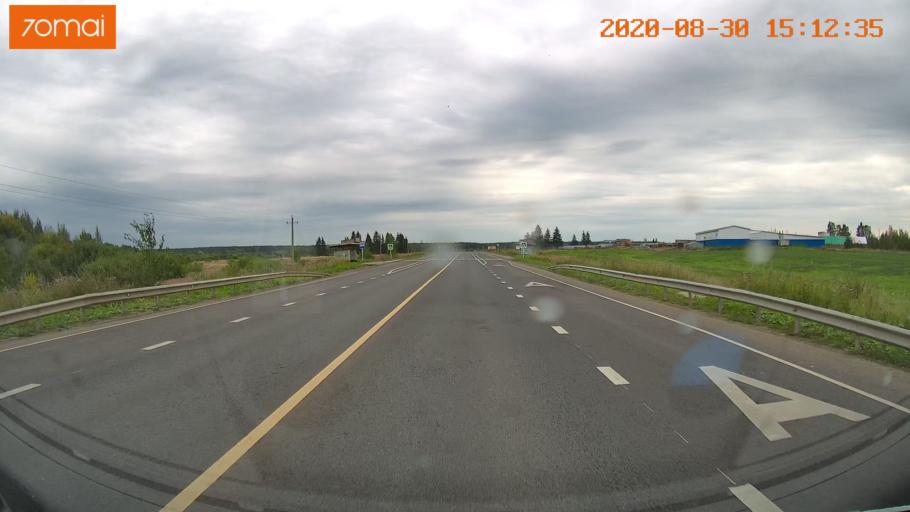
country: RU
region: Ivanovo
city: Vichuga
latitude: 57.1888
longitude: 41.8815
